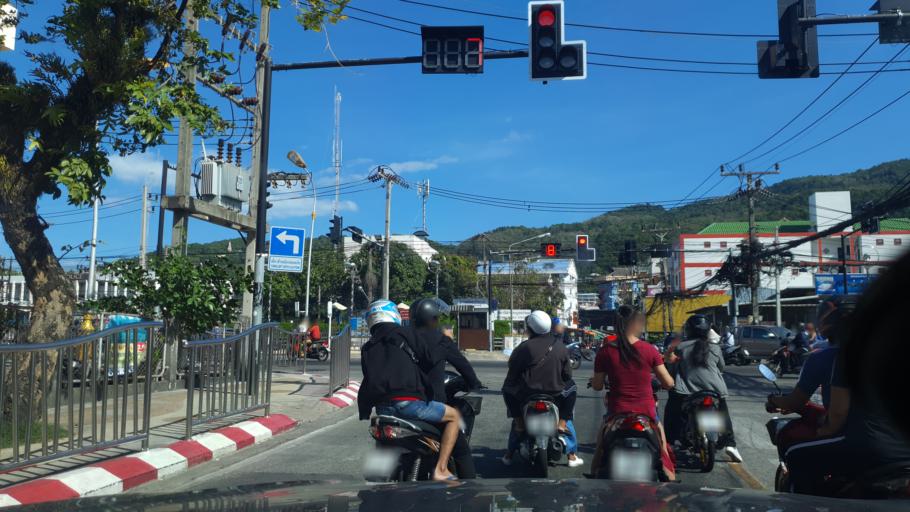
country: TH
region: Phuket
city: Patong
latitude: 7.8967
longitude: 98.3020
